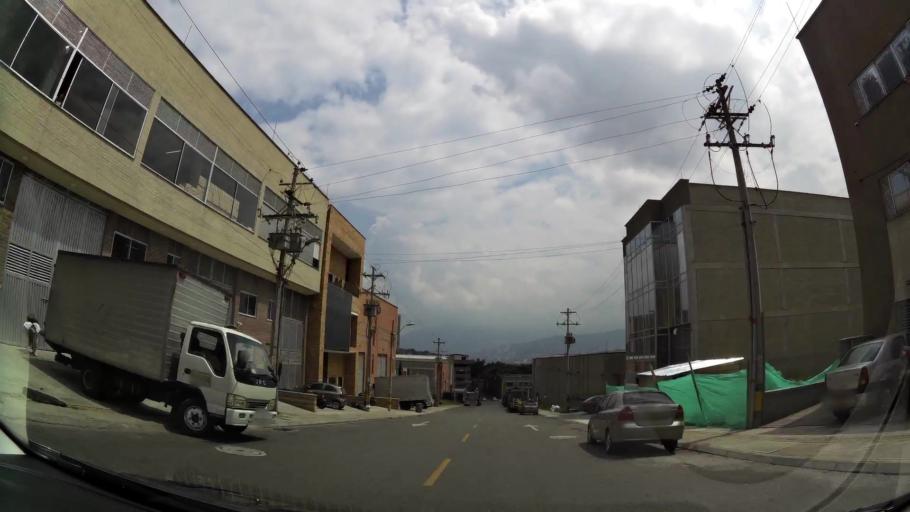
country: CO
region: Antioquia
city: Itagui
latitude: 6.1878
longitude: -75.6009
